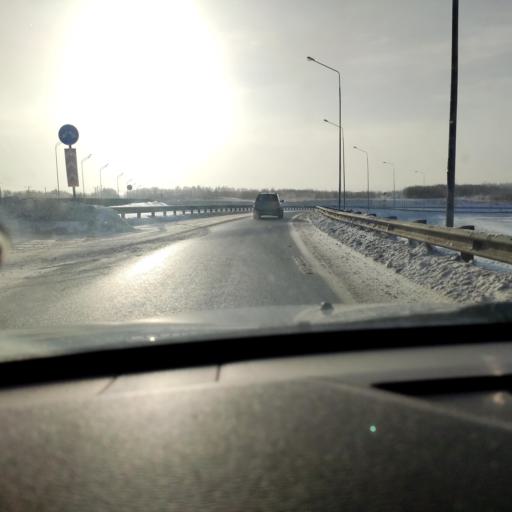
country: RU
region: Samara
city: Smyshlyayevka
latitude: 53.1508
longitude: 50.3830
